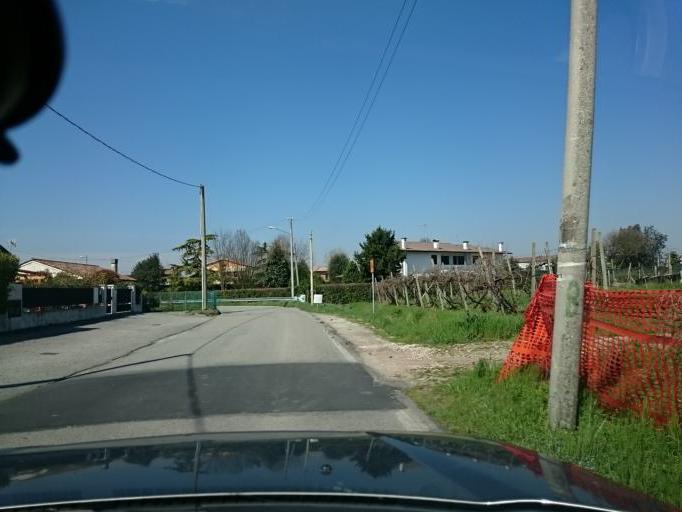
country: IT
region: Veneto
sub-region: Provincia di Padova
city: Albignasego
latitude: 45.3522
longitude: 11.8986
